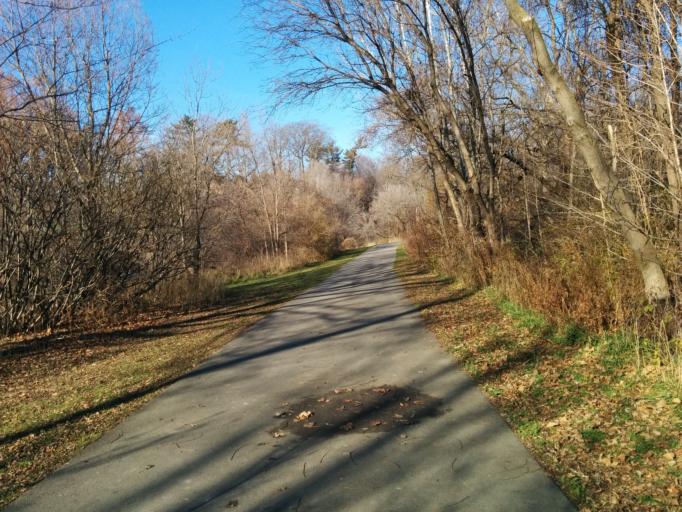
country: CA
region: Ontario
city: Etobicoke
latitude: 43.5914
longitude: -79.5490
